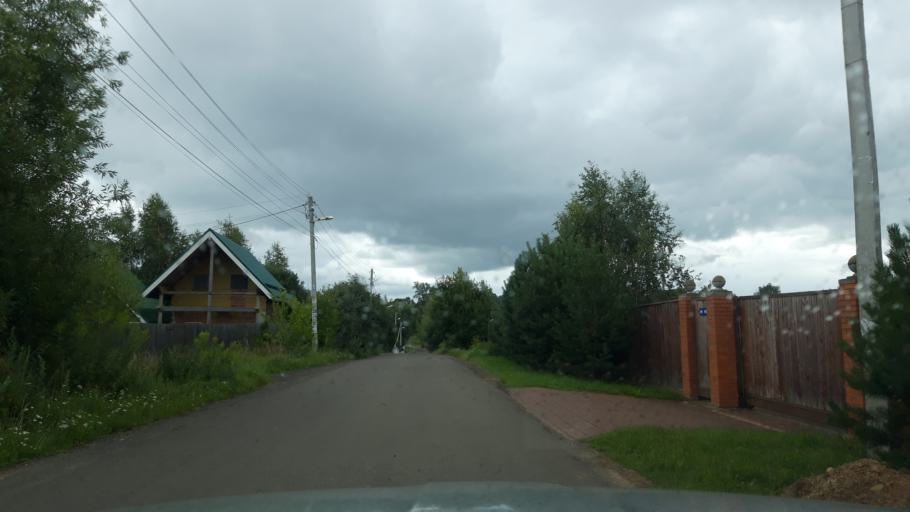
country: RU
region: Moskovskaya
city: Peshki
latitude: 56.0987
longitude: 37.0664
